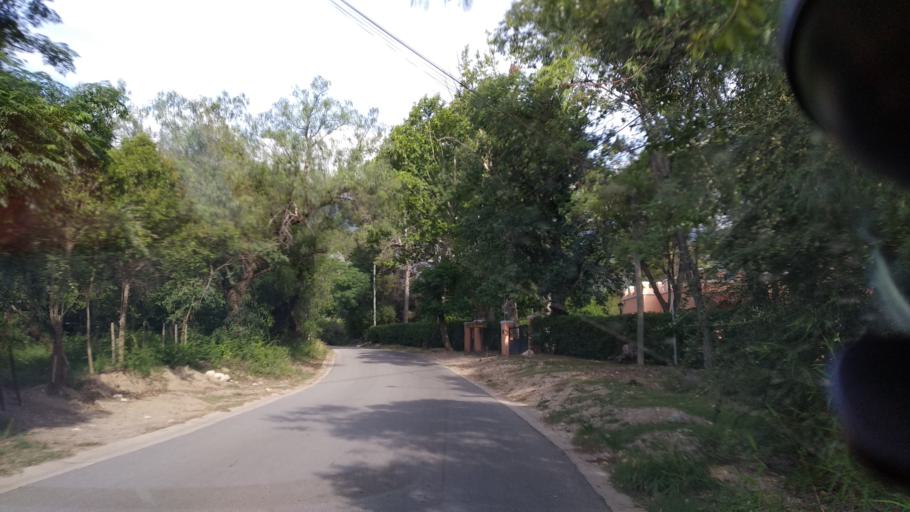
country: AR
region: Cordoba
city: Villa Las Rosas
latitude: -32.0266
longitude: -65.0134
